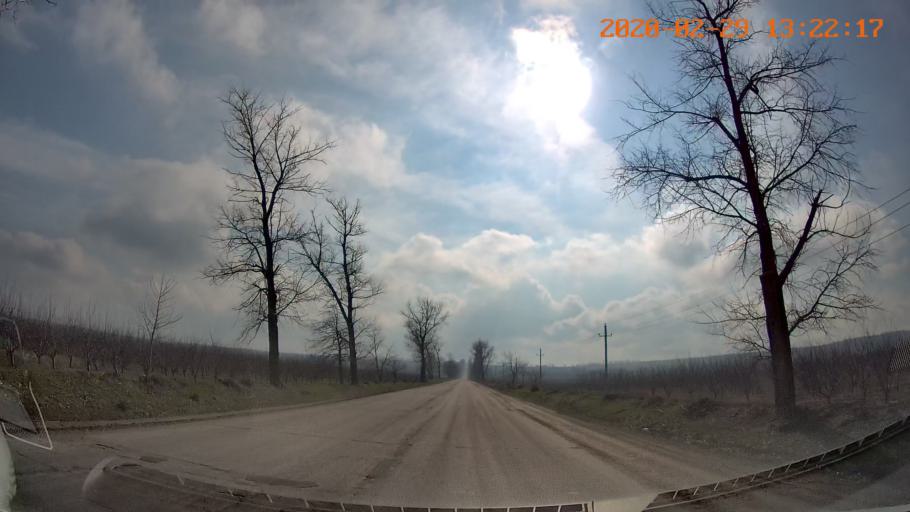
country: MD
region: Telenesti
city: Camenca
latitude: 47.9622
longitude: 28.6282
